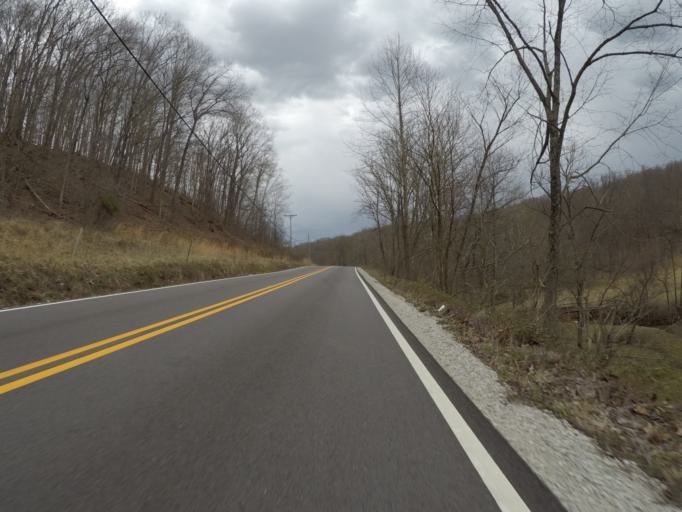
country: US
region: Ohio
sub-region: Lawrence County
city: Burlington
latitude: 38.4526
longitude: -82.5193
